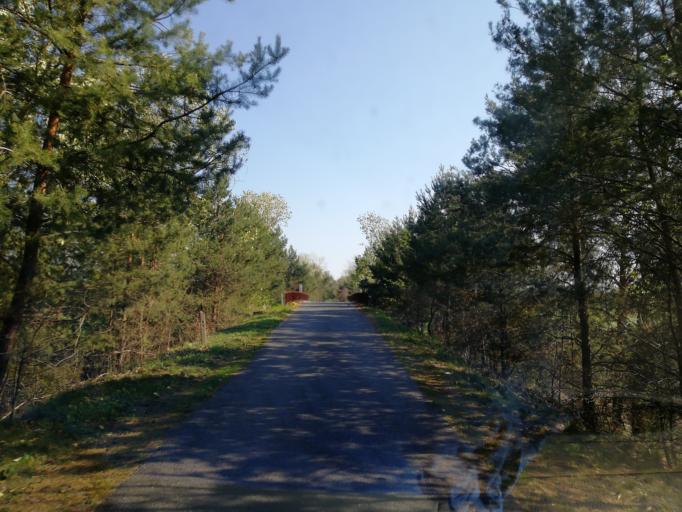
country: DE
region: Brandenburg
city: Bronkow
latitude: 51.6621
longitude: 13.8594
